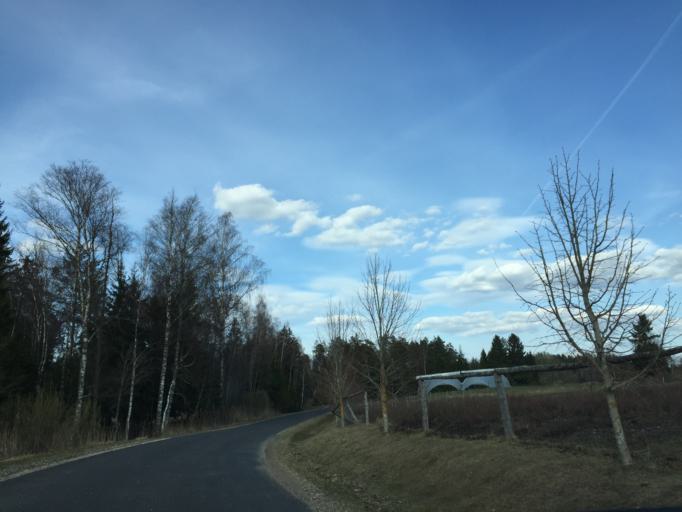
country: EE
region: Tartu
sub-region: Noo vald
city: Noo
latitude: 58.1254
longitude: 26.5759
